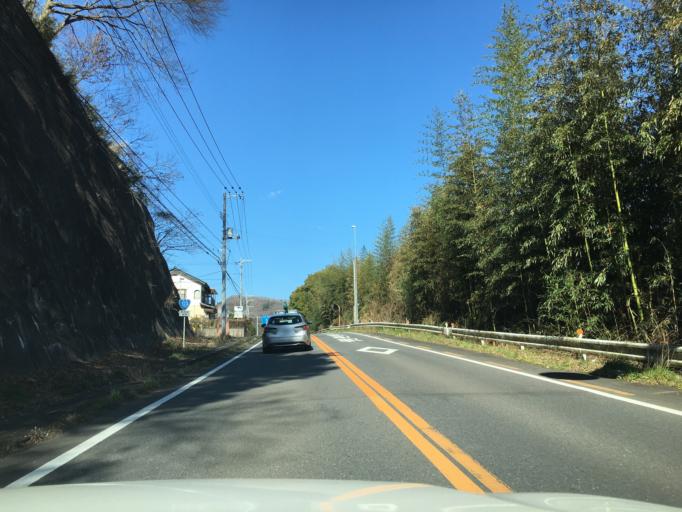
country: JP
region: Tochigi
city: Motegi
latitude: 36.5592
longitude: 140.2392
